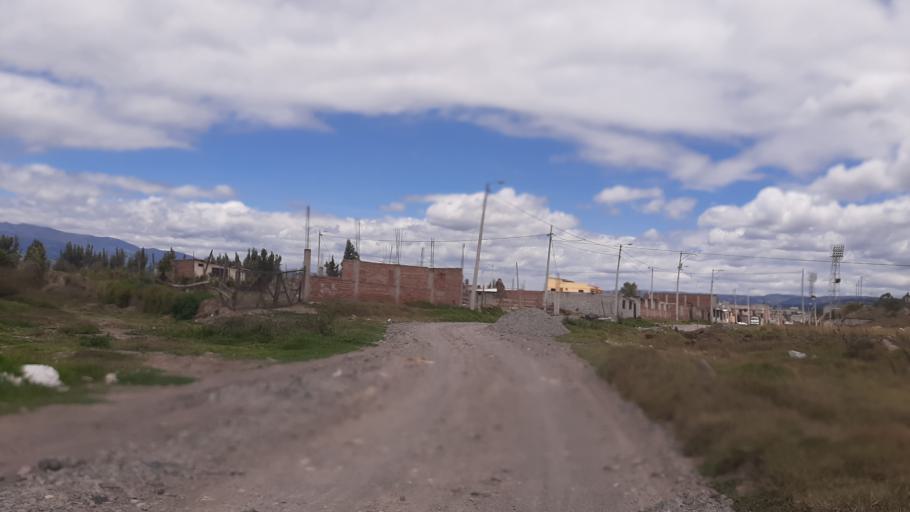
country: EC
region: Chimborazo
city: Riobamba
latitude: -1.6510
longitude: -78.6400
